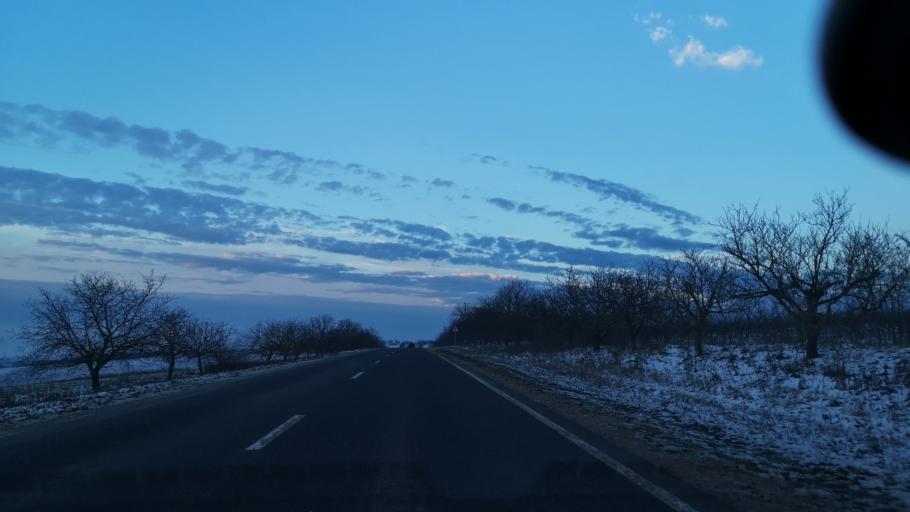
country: MD
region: Rezina
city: Saharna
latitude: 47.6147
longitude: 28.8317
